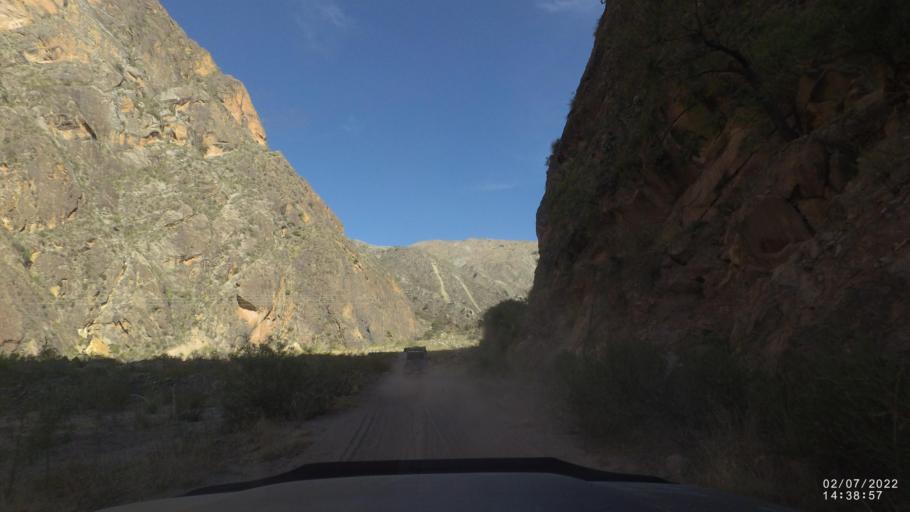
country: BO
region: Cochabamba
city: Irpa Irpa
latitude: -17.8457
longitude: -66.4191
